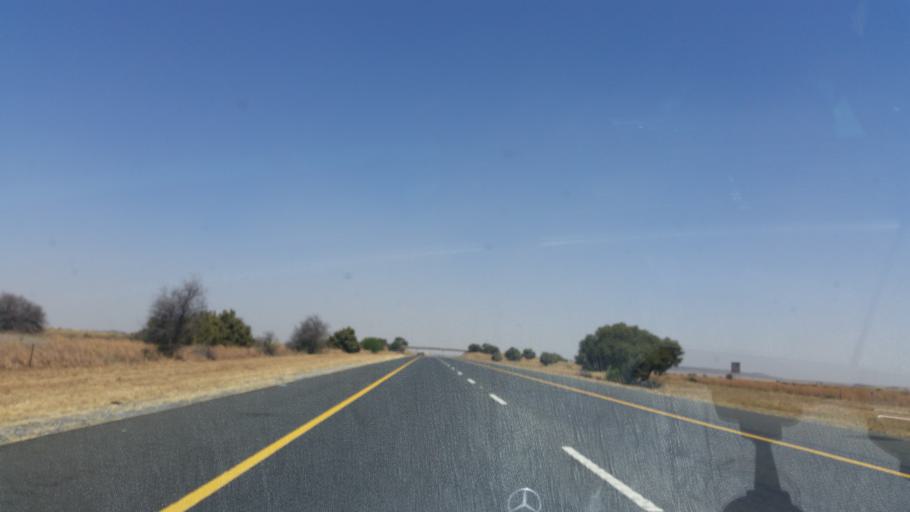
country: ZA
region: Orange Free State
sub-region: Lejweleputswa District Municipality
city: Winburg
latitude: -28.6507
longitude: 26.8754
